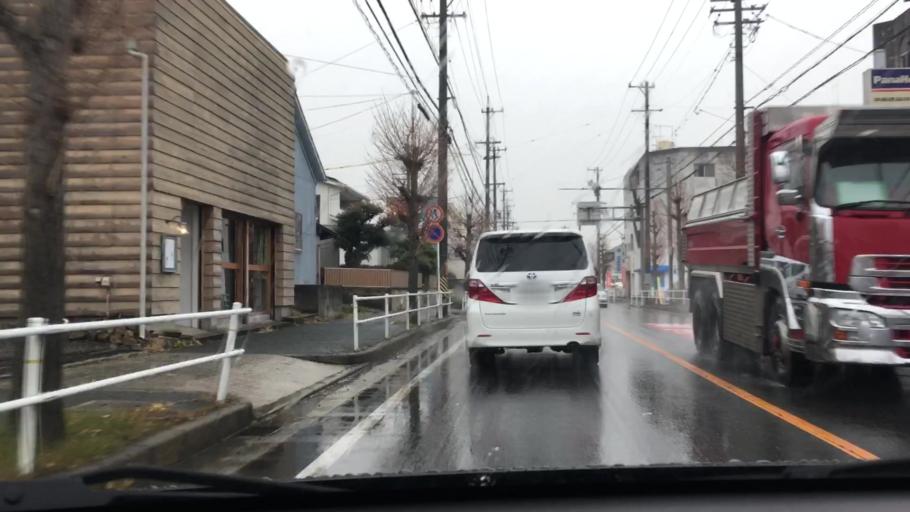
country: JP
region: Aichi
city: Gamagori
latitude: 34.8224
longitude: 137.2357
